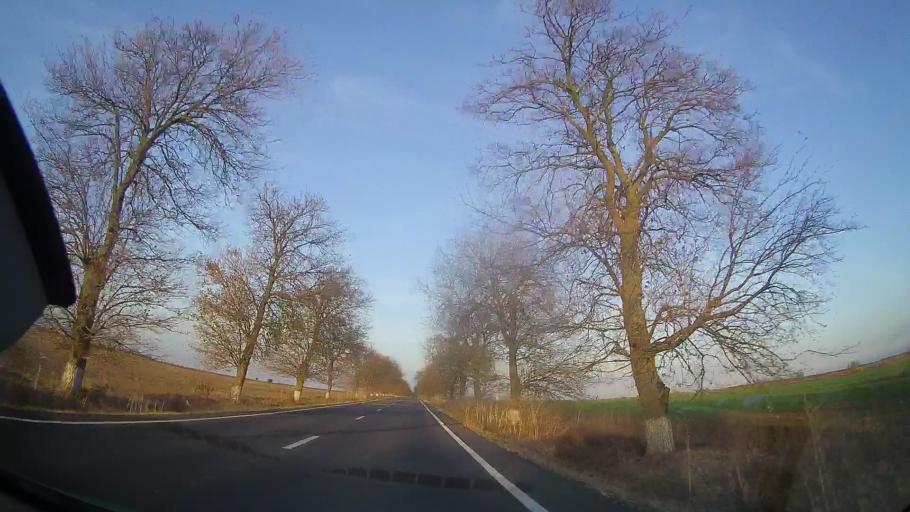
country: RO
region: Constanta
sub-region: Comuna Amzacea
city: Amzacea
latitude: 43.9486
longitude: 28.3798
